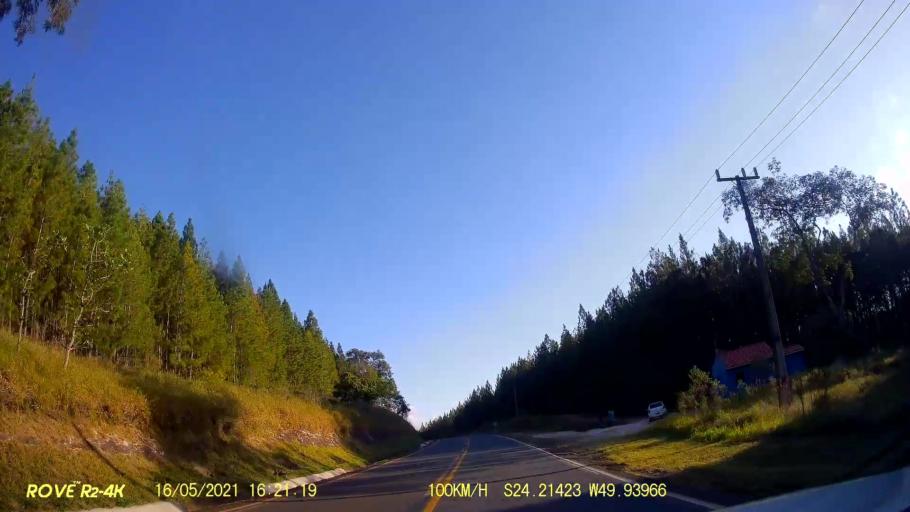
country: BR
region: Parana
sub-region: Jaguariaiva
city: Jaguariaiva
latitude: -24.2144
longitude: -49.9399
